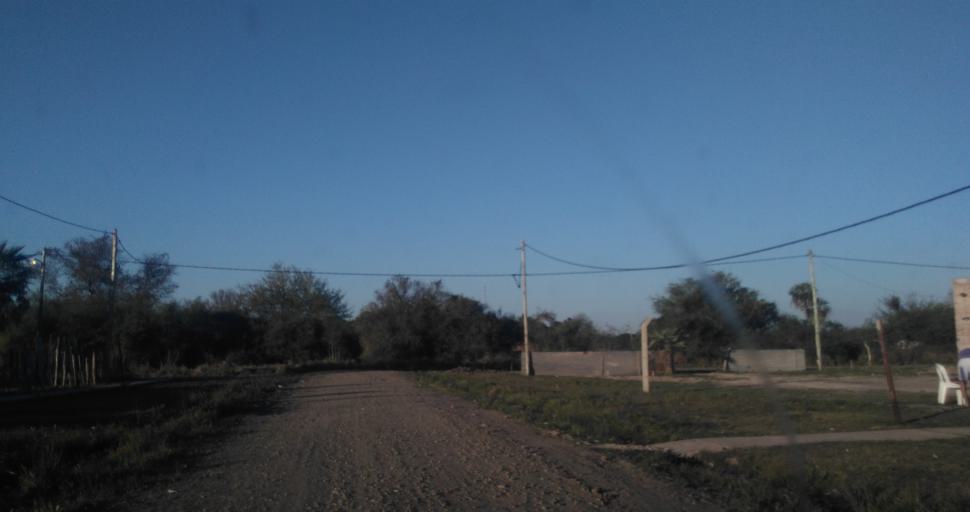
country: AR
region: Chaco
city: Resistencia
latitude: -27.4716
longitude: -59.0215
